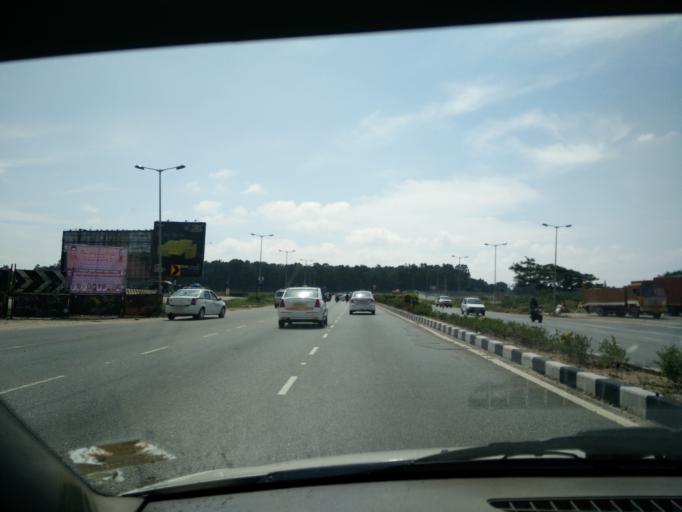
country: IN
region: Karnataka
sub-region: Bangalore Urban
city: Yelahanka
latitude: 13.1390
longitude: 77.6175
